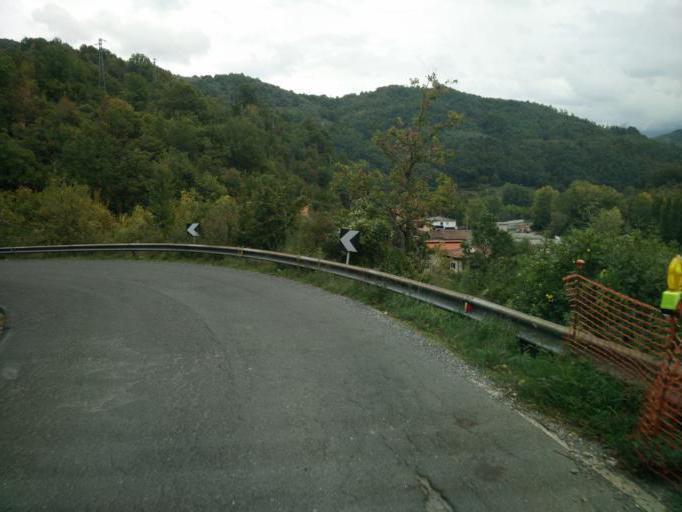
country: IT
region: Tuscany
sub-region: Provincia di Massa-Carrara
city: Fivizzano
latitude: 44.2048
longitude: 10.0970
